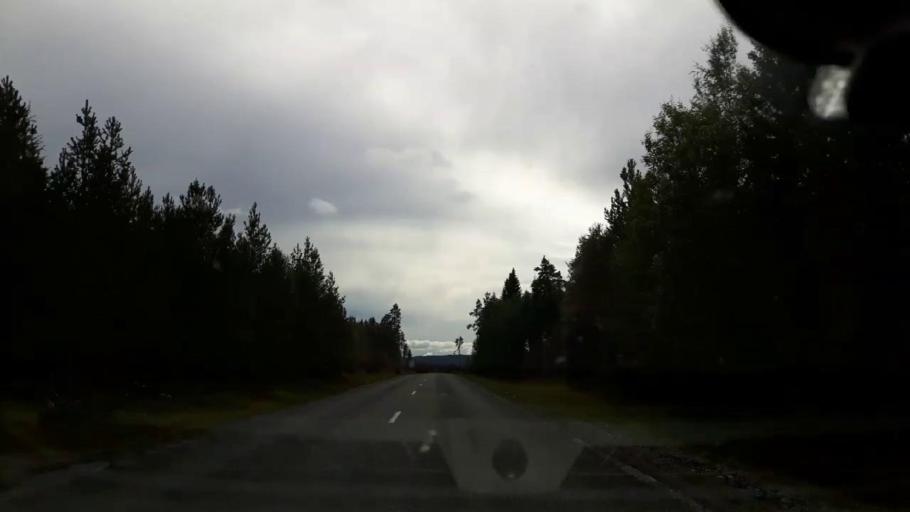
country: SE
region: Jaemtland
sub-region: Ragunda Kommun
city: Hammarstrand
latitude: 63.0729
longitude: 15.9162
